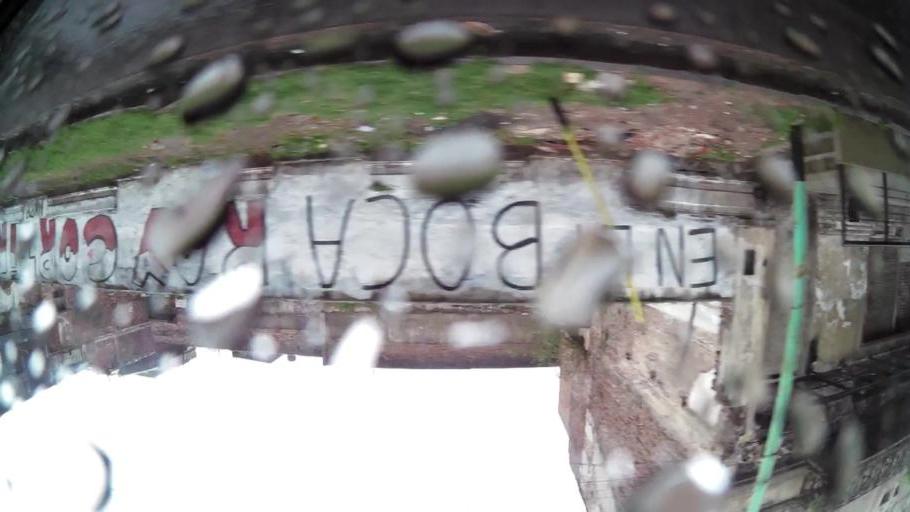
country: AR
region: Buenos Aires
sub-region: Partido de Avellaneda
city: Avellaneda
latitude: -34.6354
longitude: -58.3568
